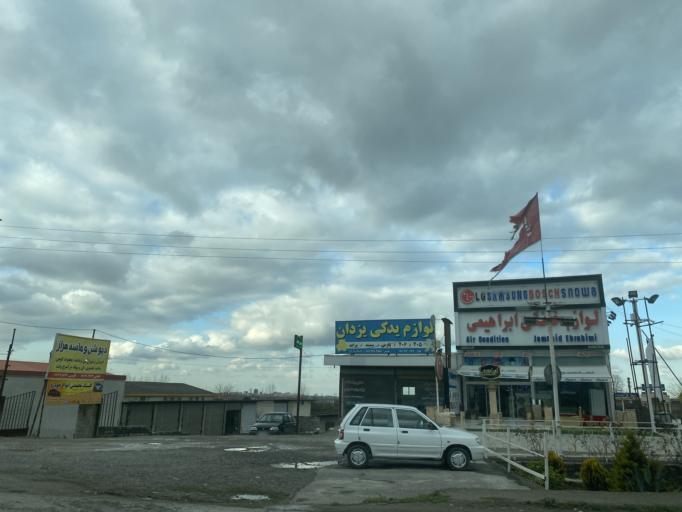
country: IR
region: Mazandaran
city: Amol
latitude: 36.4343
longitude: 52.3656
